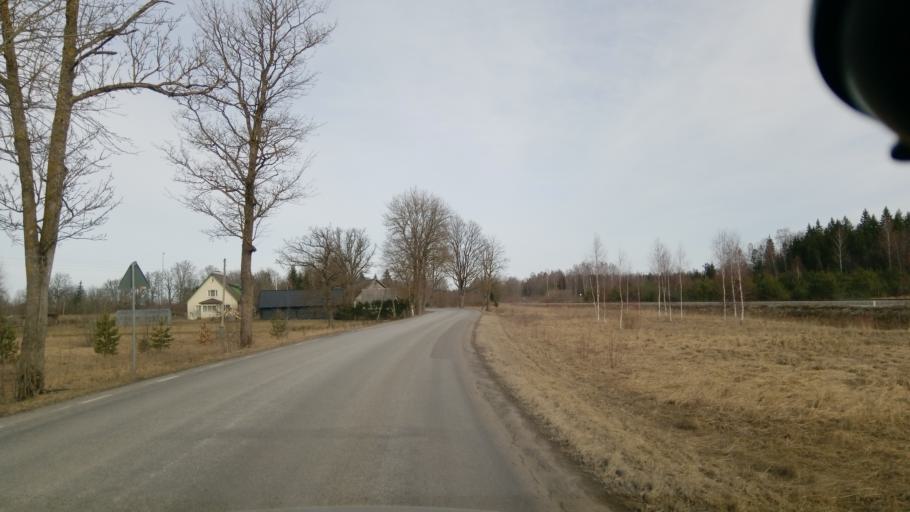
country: EE
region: Raplamaa
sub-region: Rapla vald
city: Rapla
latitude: 59.0203
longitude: 24.8375
